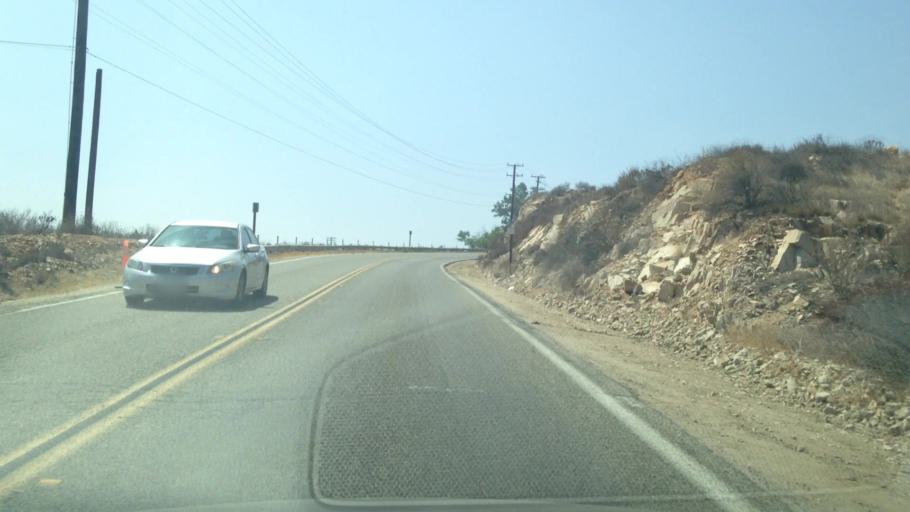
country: US
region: California
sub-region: Riverside County
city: El Cerrito
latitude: 33.8545
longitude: -117.4546
